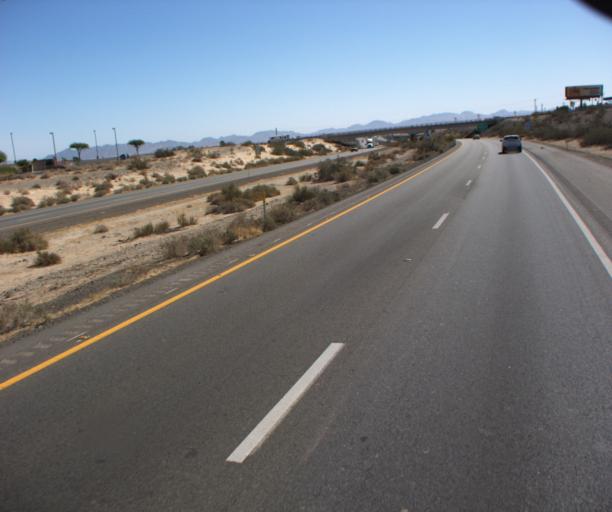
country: US
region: Arizona
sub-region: Yuma County
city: Yuma
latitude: 32.6931
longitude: -114.6018
